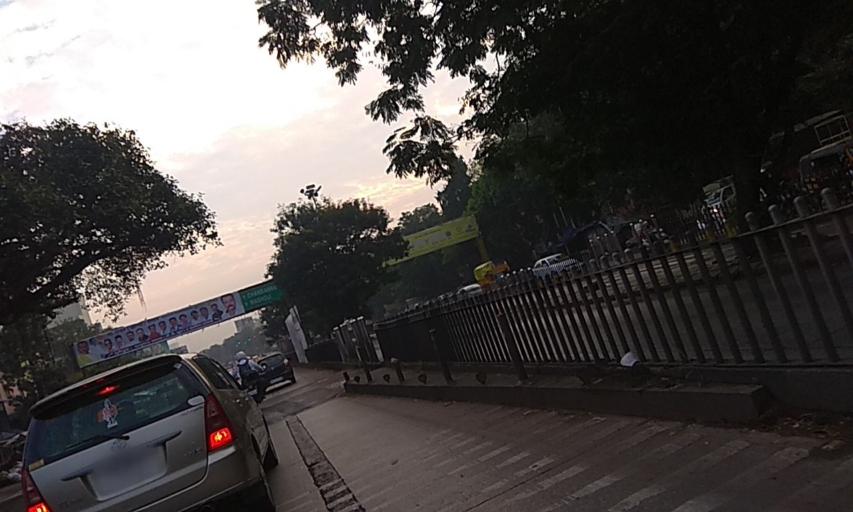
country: IN
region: Maharashtra
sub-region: Pune Division
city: Shivaji Nagar
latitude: 18.5454
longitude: 73.8867
